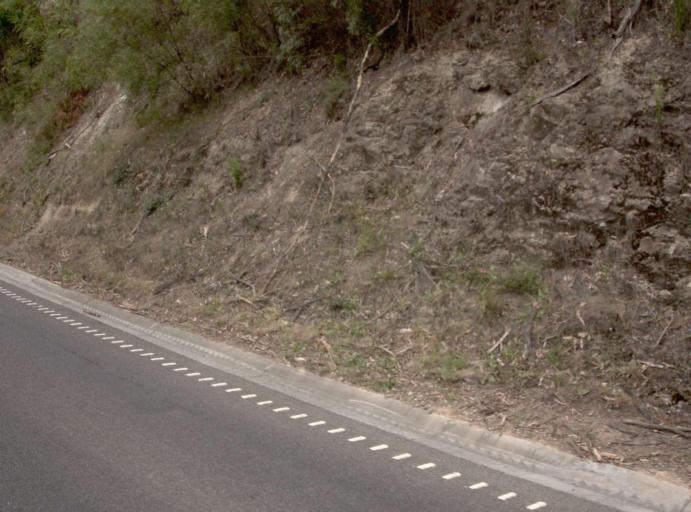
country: AU
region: Victoria
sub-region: Yarra Ranges
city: Yarra Glen
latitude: -37.5457
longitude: 145.4163
